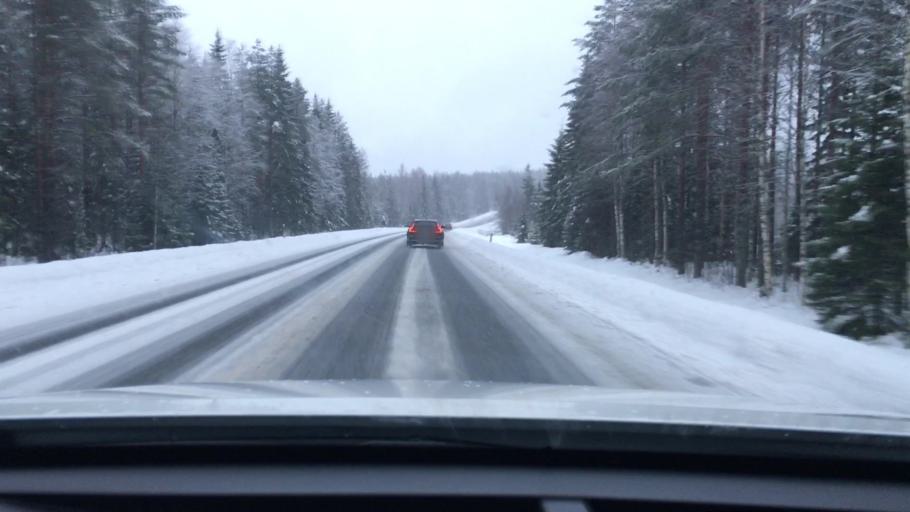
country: FI
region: Northern Savo
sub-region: Ylae-Savo
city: Sonkajaervi
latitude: 63.7712
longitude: 27.4149
